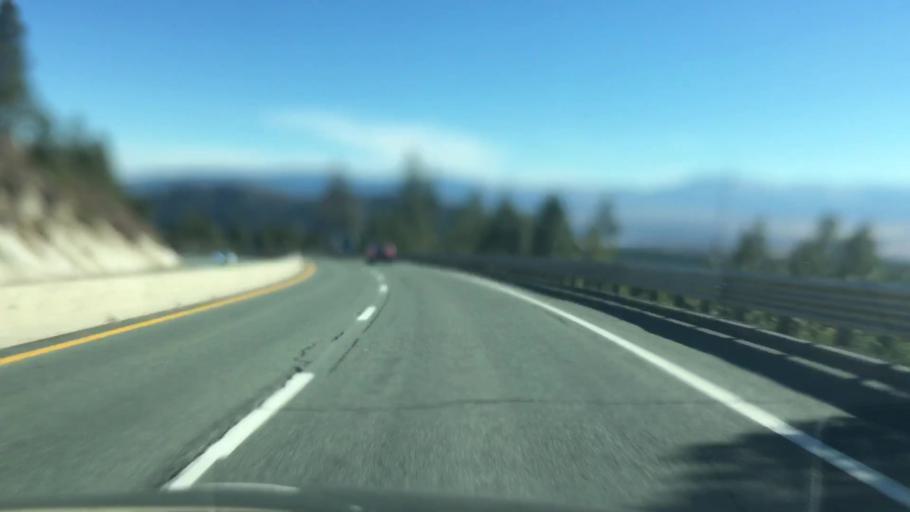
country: US
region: Nevada
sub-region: Douglas County
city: Indian Hills
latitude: 39.1144
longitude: -119.8682
